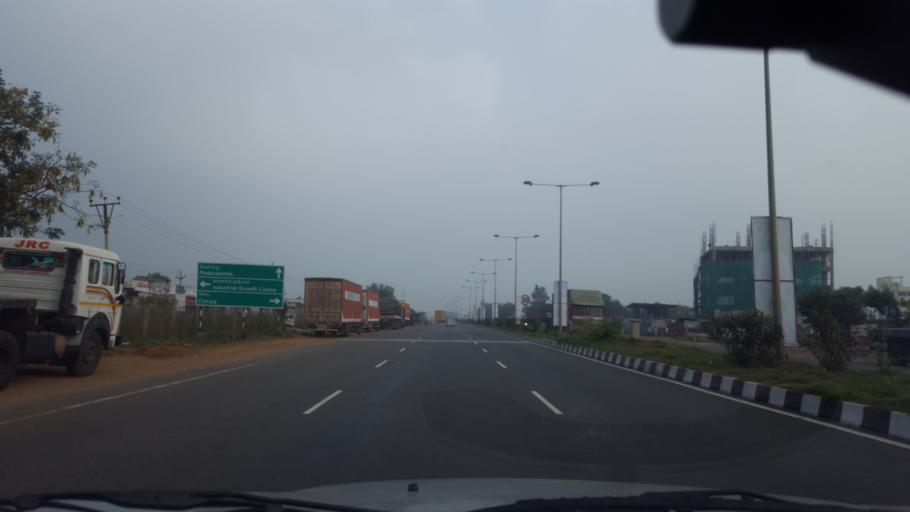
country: IN
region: Andhra Pradesh
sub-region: Prakasam
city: Addanki
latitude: 15.6839
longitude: 80.0179
